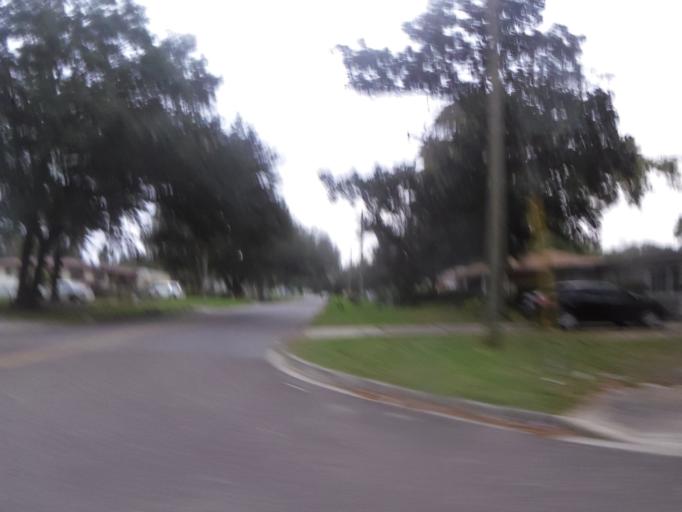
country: US
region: Florida
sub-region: Clay County
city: Bellair-Meadowbrook Terrace
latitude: 30.2769
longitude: -81.7477
